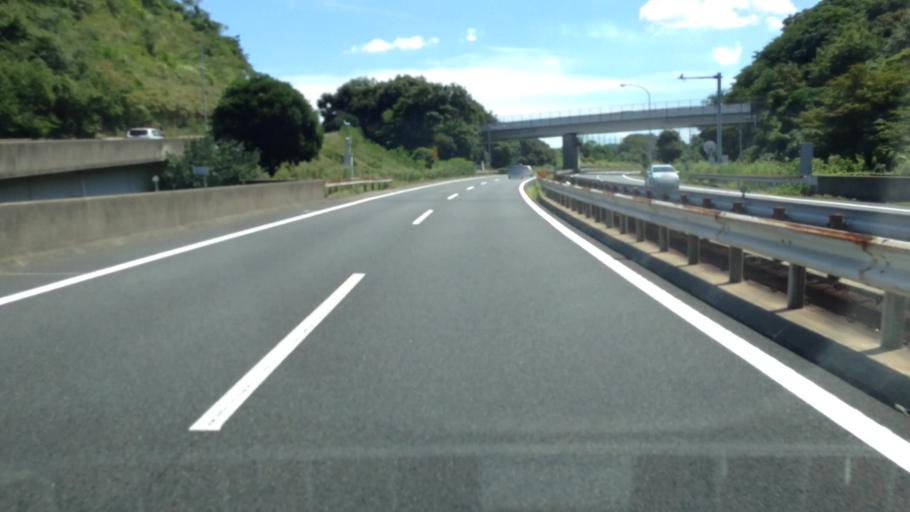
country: JP
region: Kanagawa
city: Yokosuka
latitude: 35.2783
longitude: 139.6331
